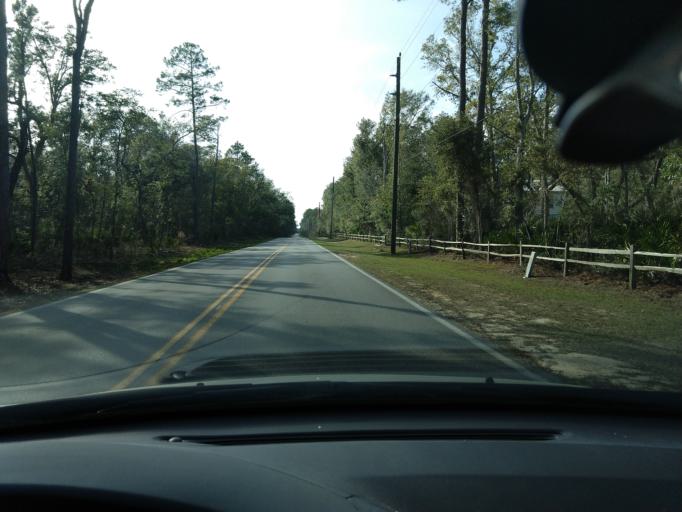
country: US
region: Florida
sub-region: Walton County
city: Seaside
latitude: 30.3730
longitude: -86.1415
